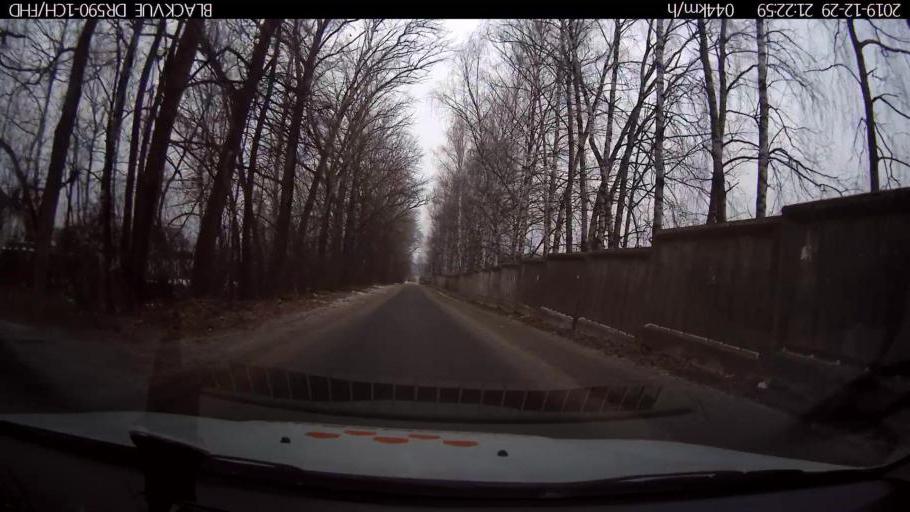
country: RU
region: Nizjnij Novgorod
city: Afonino
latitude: 56.2191
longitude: 44.0368
